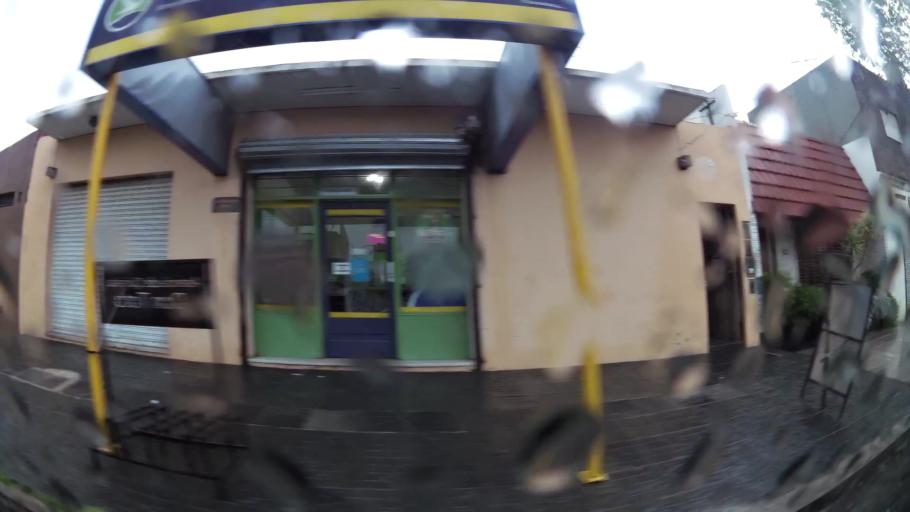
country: AR
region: Buenos Aires
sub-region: Partido de Lanus
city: Lanus
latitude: -34.7152
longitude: -58.4081
